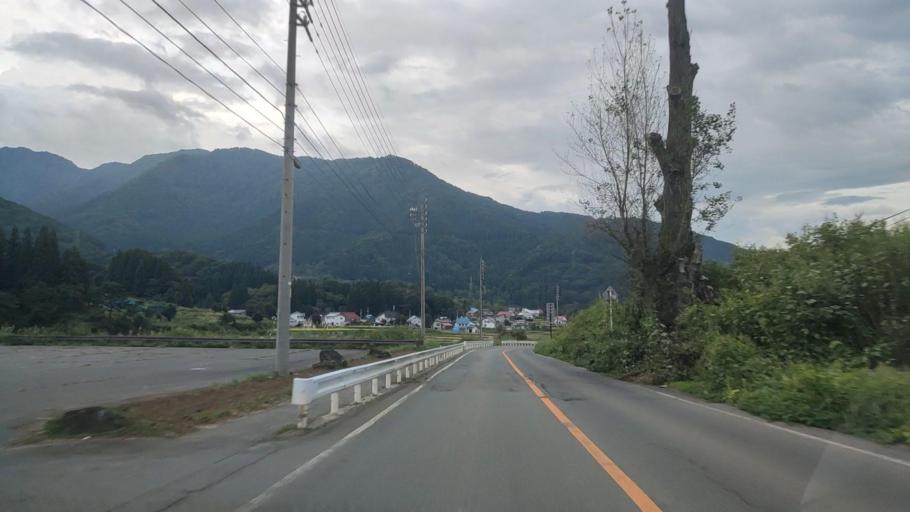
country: JP
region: Nagano
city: Iiyama
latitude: 36.8856
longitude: 138.4110
